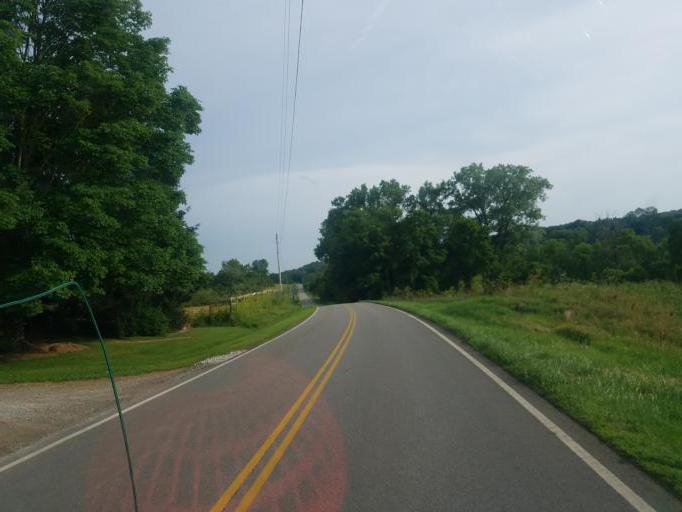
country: US
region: Ohio
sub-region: Ashland County
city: Loudonville
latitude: 40.7340
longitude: -82.2885
